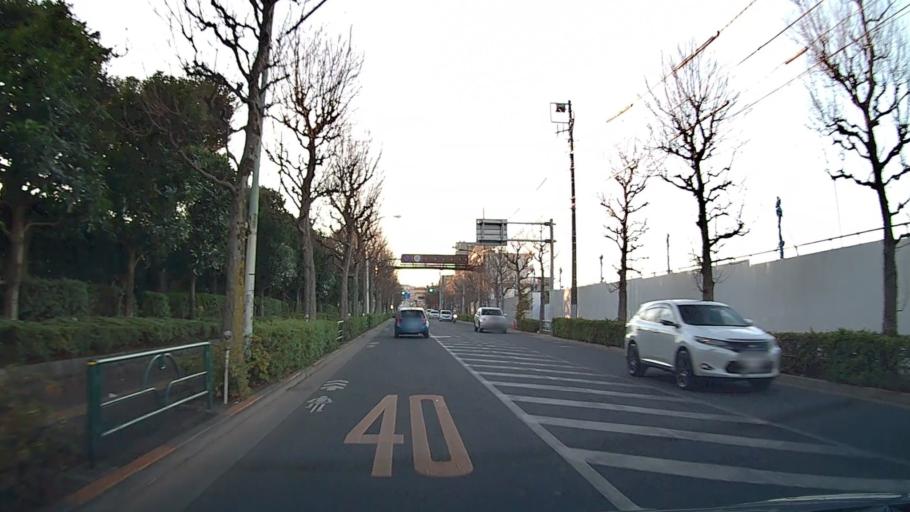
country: JP
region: Tokyo
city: Musashino
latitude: 35.7280
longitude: 139.6120
